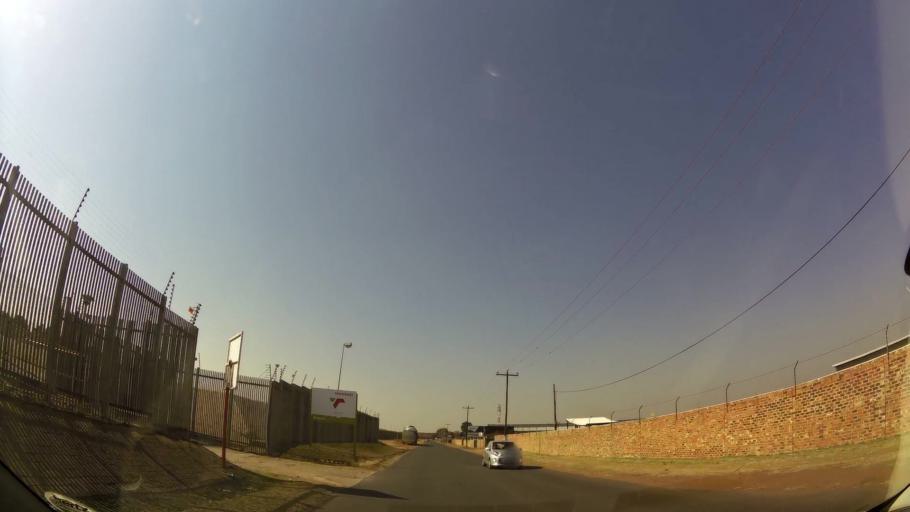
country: ZA
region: Gauteng
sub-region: Ekurhuleni Metropolitan Municipality
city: Boksburg
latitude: -26.1660
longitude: 28.2383
